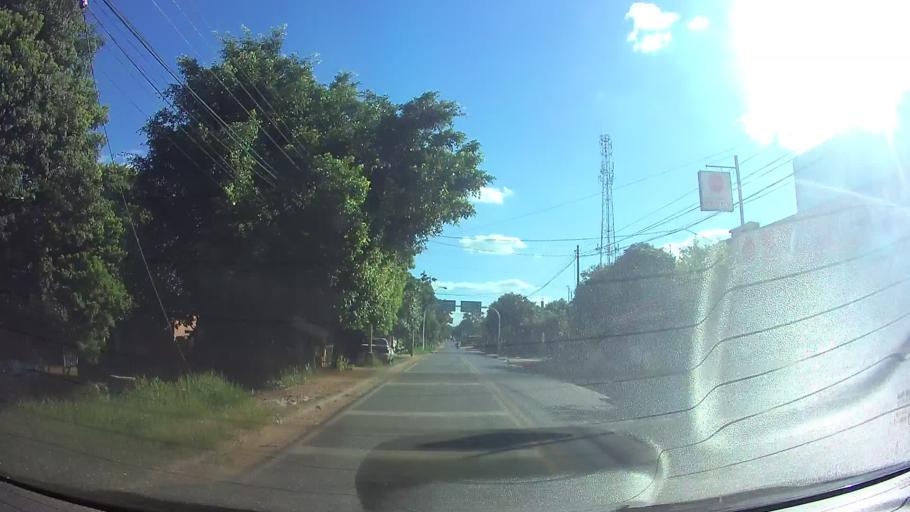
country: PY
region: Cordillera
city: Caacupe
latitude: -25.3747
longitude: -57.1377
